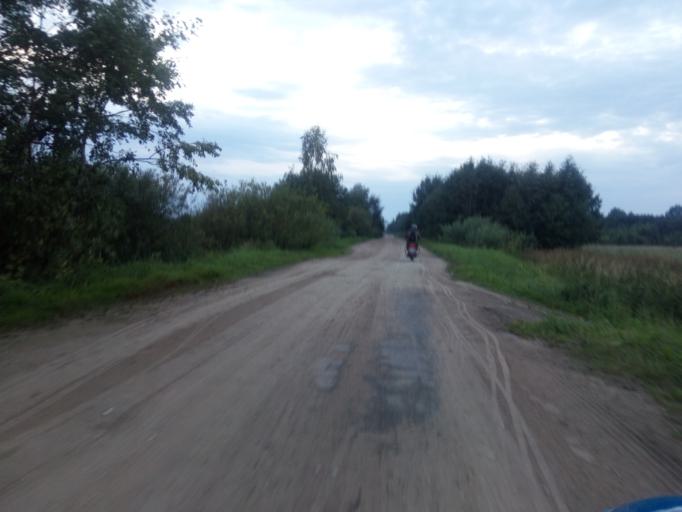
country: BY
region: Vitebsk
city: Dzisna
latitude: 55.6713
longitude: 28.3126
